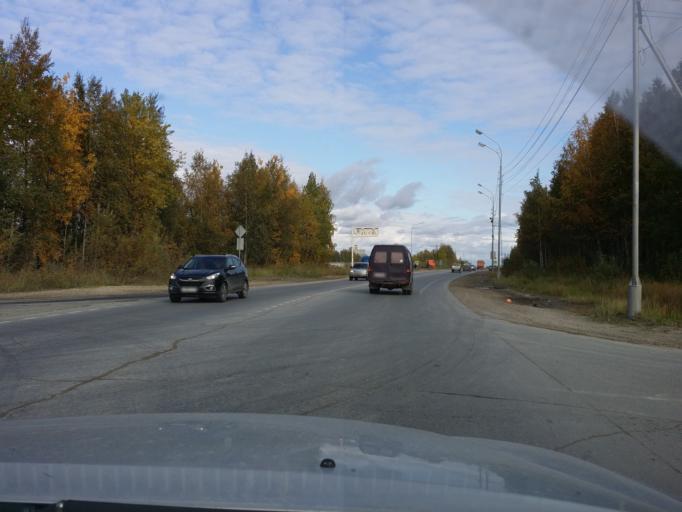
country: RU
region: Khanty-Mansiyskiy Avtonomnyy Okrug
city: Megion
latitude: 61.0499
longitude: 76.1118
